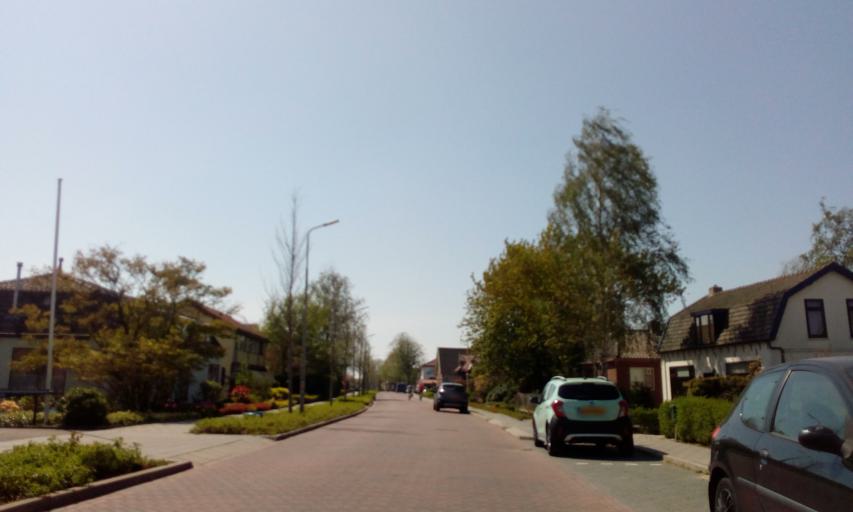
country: NL
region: South Holland
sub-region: Gemeente Kaag en Braassem
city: Leimuiden
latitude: 52.1901
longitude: 4.7026
